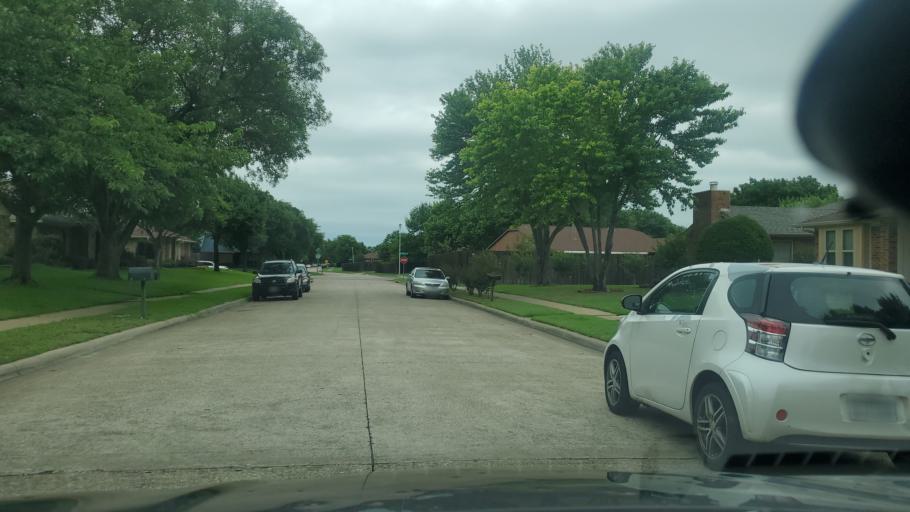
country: US
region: Texas
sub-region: Dallas County
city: Garland
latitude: 32.9409
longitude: -96.6334
